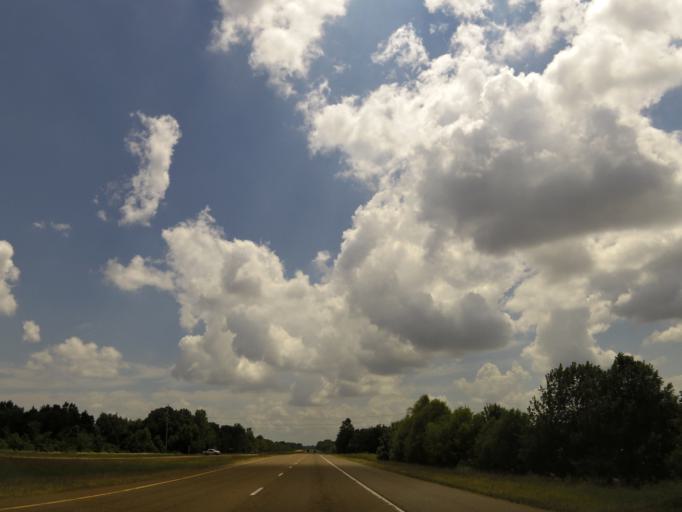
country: US
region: Tennessee
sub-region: Dyer County
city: Dyersburg
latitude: 36.0089
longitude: -89.3415
